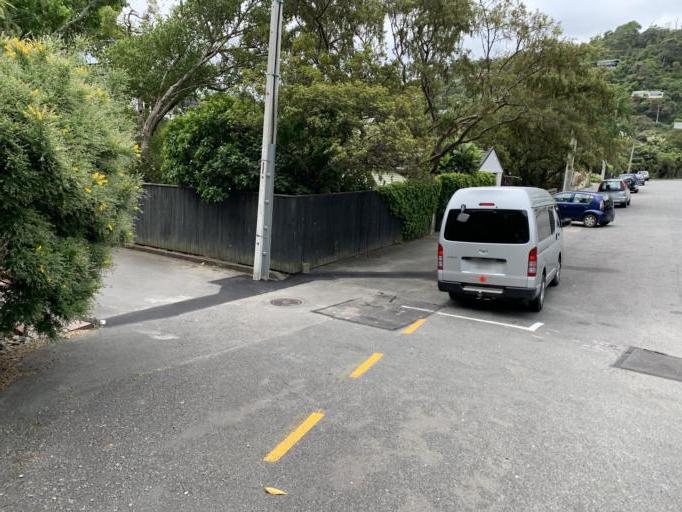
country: NZ
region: Wellington
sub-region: Lower Hutt City
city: Lower Hutt
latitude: -41.2794
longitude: 174.9086
